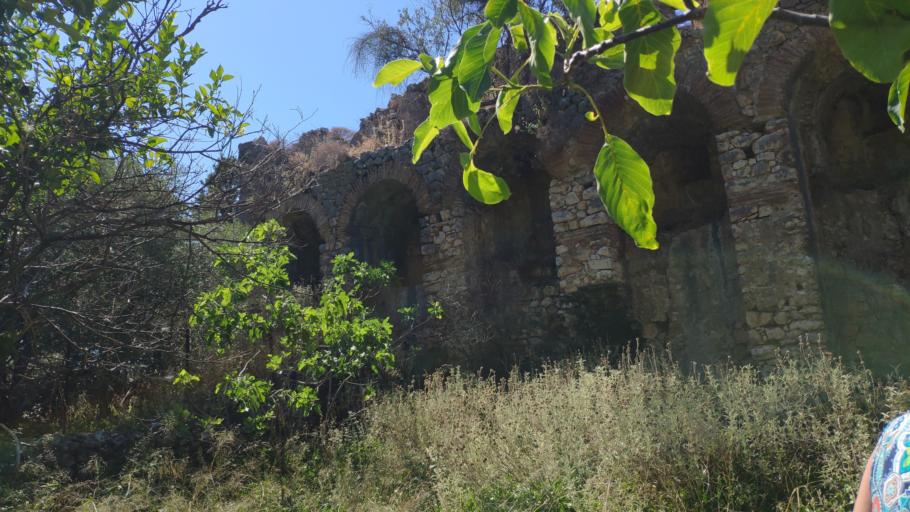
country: GR
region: West Greece
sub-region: Nomos Aitolias kai Akarnanias
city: Kandila
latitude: 38.6515
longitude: 20.9432
